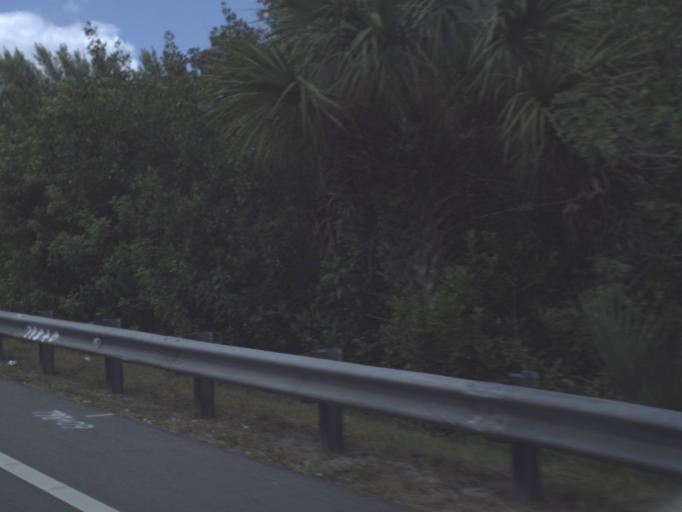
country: US
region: Florida
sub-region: Collier County
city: Marco
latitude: 25.9136
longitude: -81.3713
